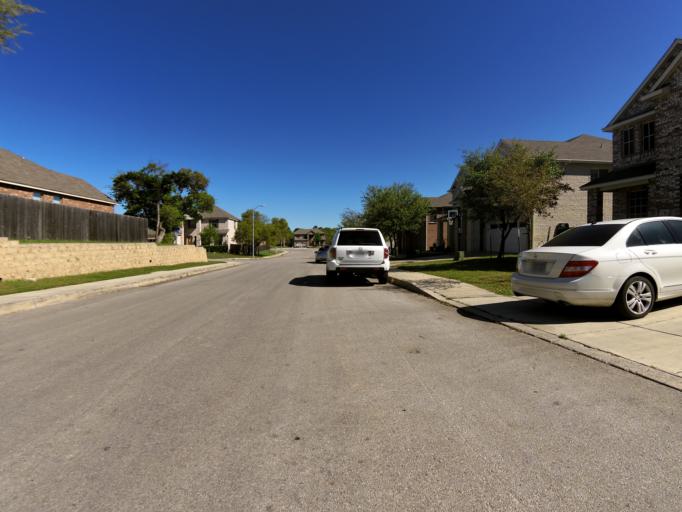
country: US
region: Texas
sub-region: Bexar County
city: Cross Mountain
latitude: 29.6750
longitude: -98.6415
